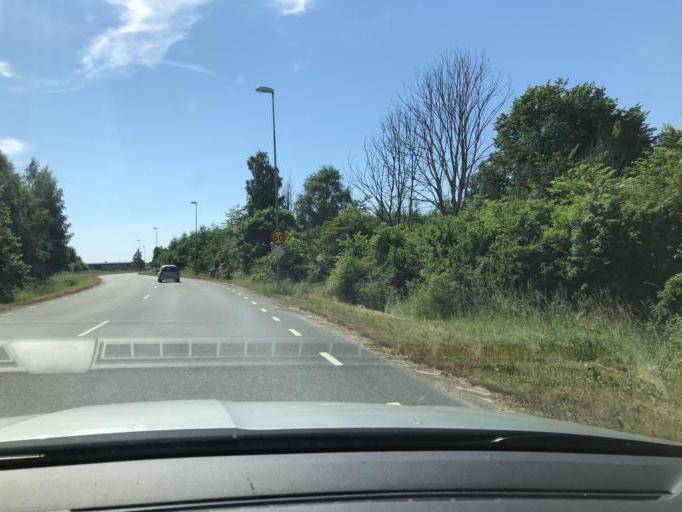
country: SE
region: Skane
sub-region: Bromolla Kommun
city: Bromoella
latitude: 56.0763
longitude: 14.4979
